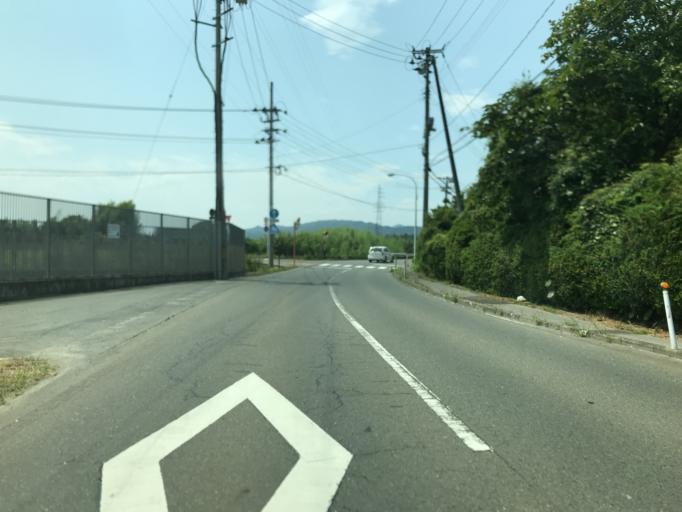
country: JP
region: Miyagi
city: Marumori
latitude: 37.7906
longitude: 140.9089
